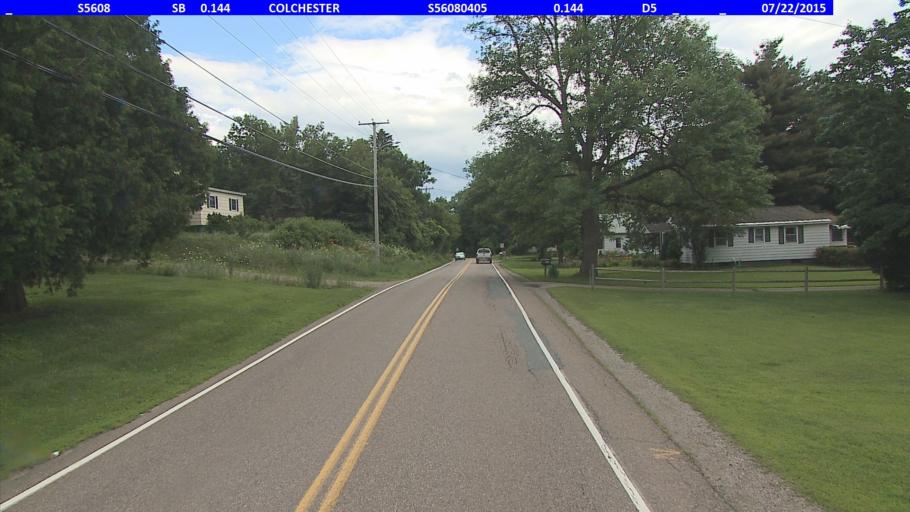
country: US
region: Vermont
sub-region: Chittenden County
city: Winooski
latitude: 44.5014
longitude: -73.1983
